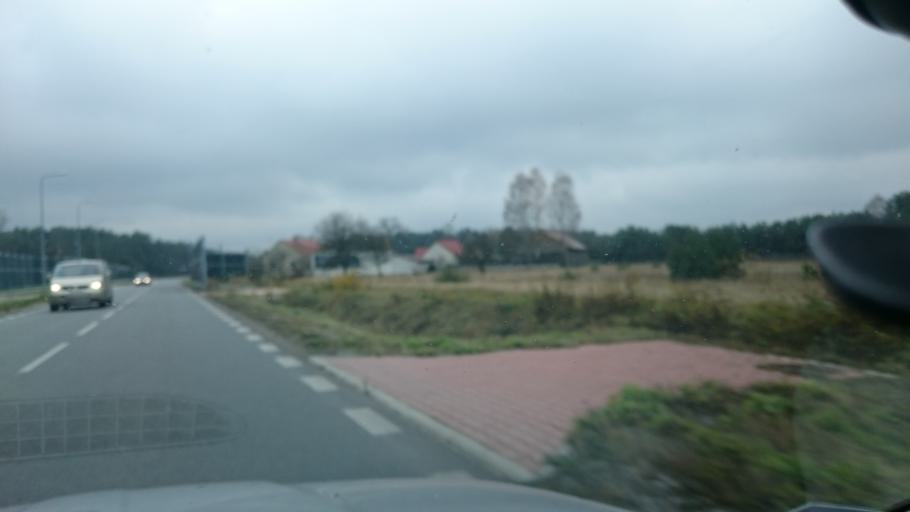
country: PL
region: Swietokrzyskie
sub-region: Powiat konecki
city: Konskie
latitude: 51.1303
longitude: 20.3607
